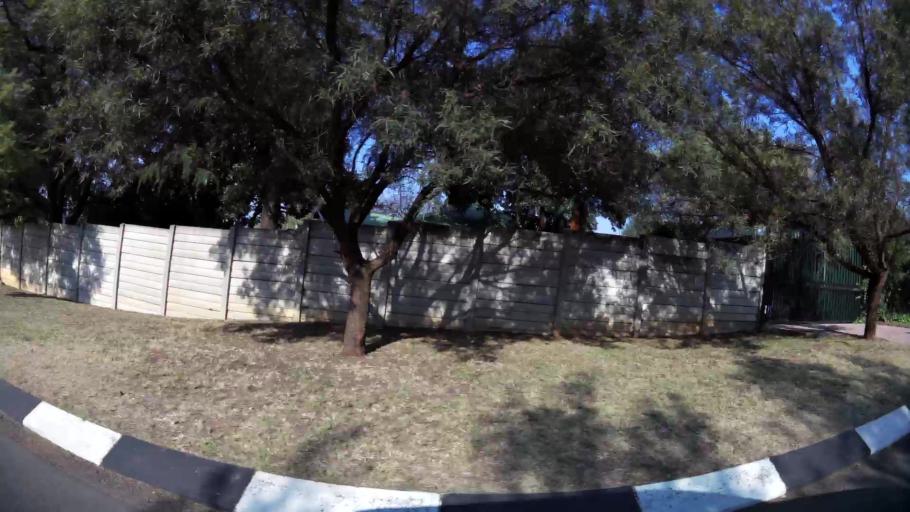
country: ZA
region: Gauteng
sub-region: City of Johannesburg Metropolitan Municipality
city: Modderfontein
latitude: -26.1011
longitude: 28.1483
